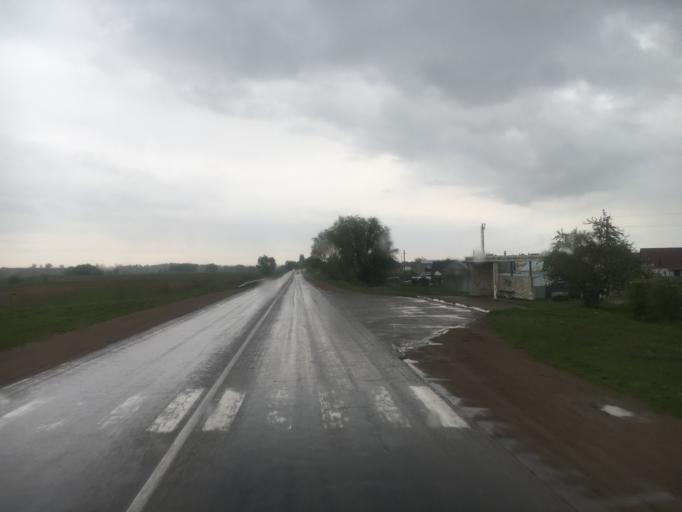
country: KZ
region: Almaty Oblysy
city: Burunday
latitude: 43.2909
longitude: 76.6733
